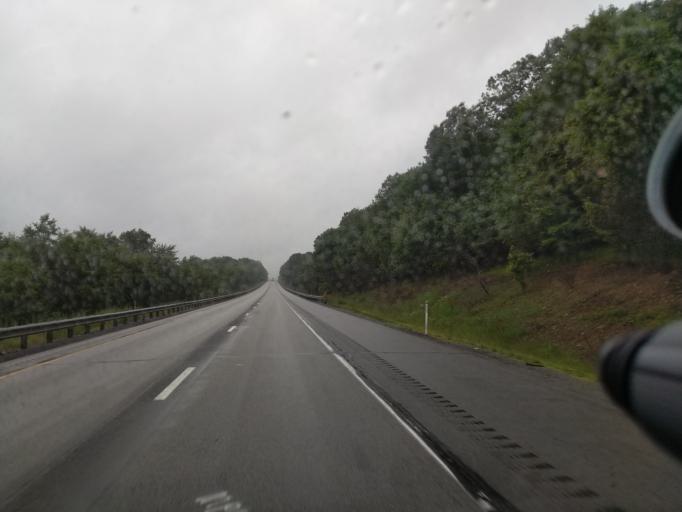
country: US
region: Pennsylvania
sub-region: Clearfield County
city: Troy
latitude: 40.9889
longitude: -78.1985
